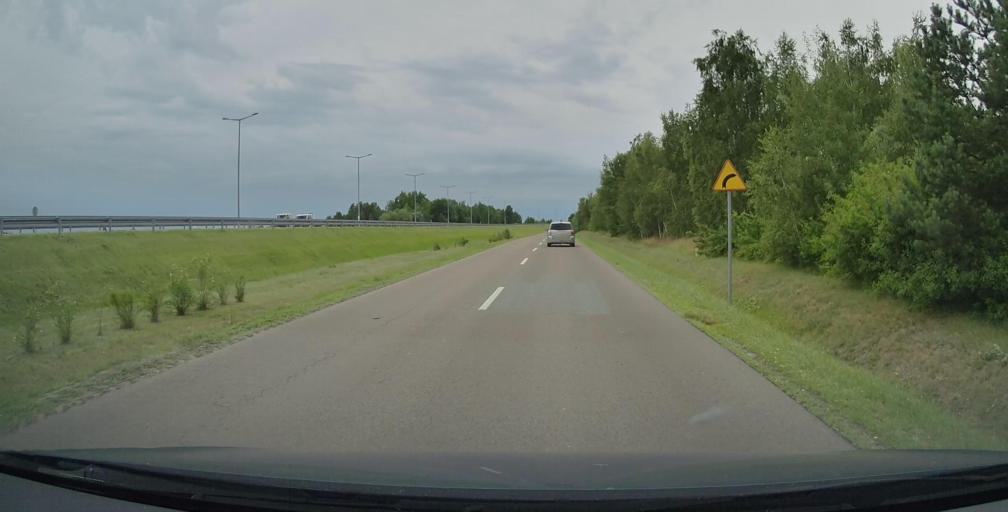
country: PL
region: Lublin Voivodeship
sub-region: Powiat bialski
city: Terespol
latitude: 52.0637
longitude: 23.6298
